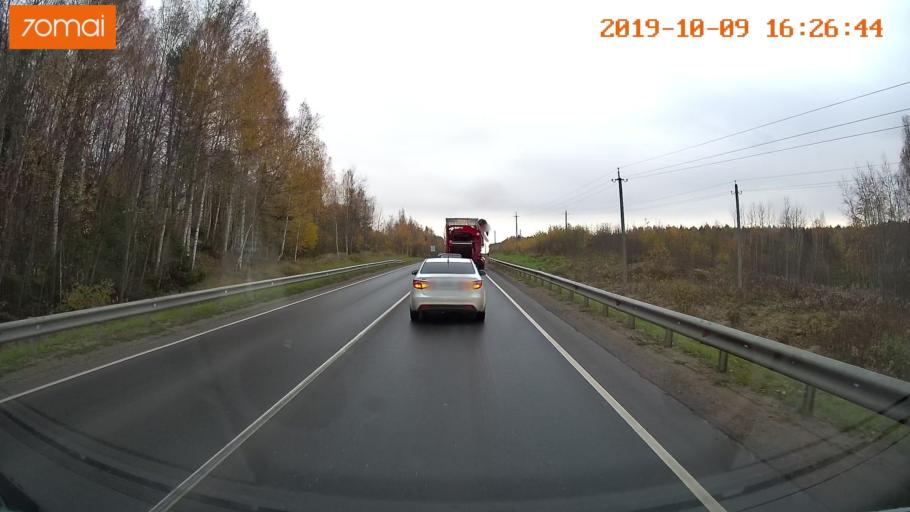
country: RU
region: Kostroma
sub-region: Kostromskoy Rayon
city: Kostroma
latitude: 57.6364
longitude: 40.9252
